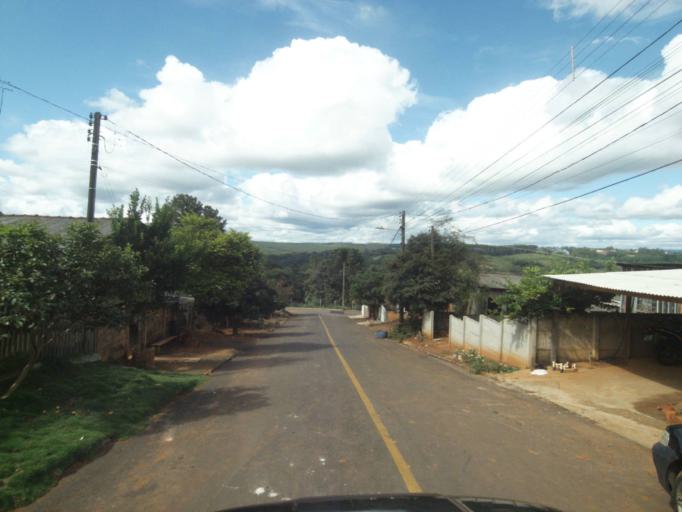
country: BR
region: Parana
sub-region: Telemaco Borba
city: Telemaco Borba
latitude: -24.3137
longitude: -50.6353
